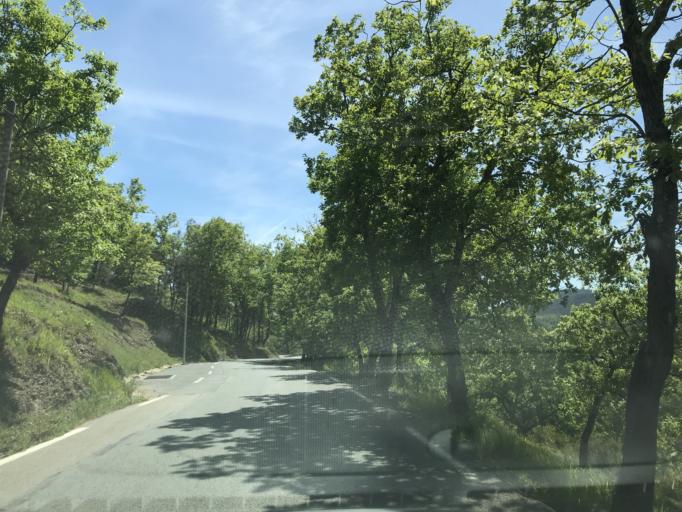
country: FR
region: Provence-Alpes-Cote d'Azur
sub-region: Departement du Var
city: Montauroux
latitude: 43.5857
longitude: 6.8164
